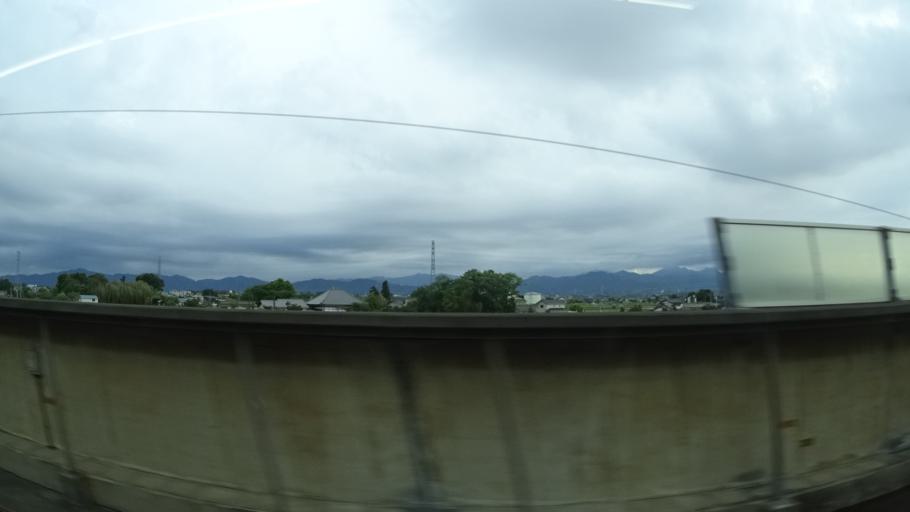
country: JP
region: Gunma
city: Fujioka
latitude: 36.2494
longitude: 139.1190
